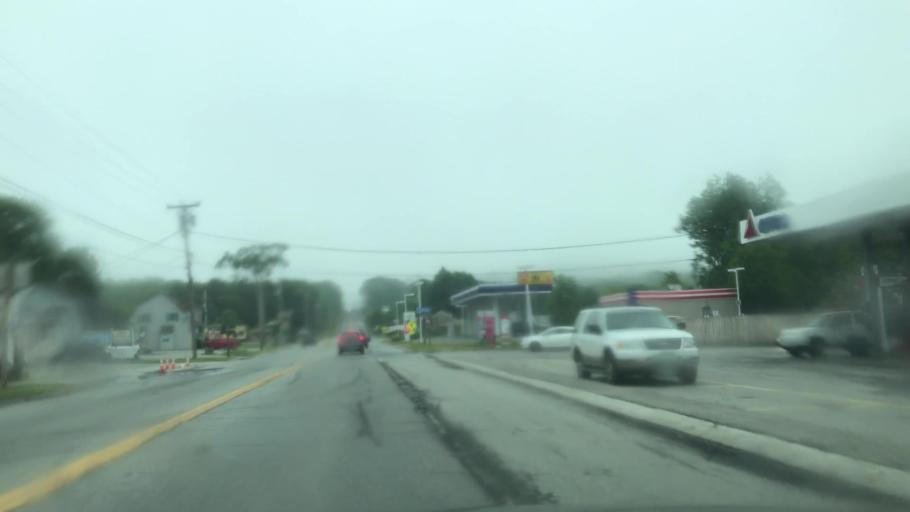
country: US
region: Maine
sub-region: Lincoln County
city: Waldoboro
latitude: 44.1017
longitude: -69.3823
